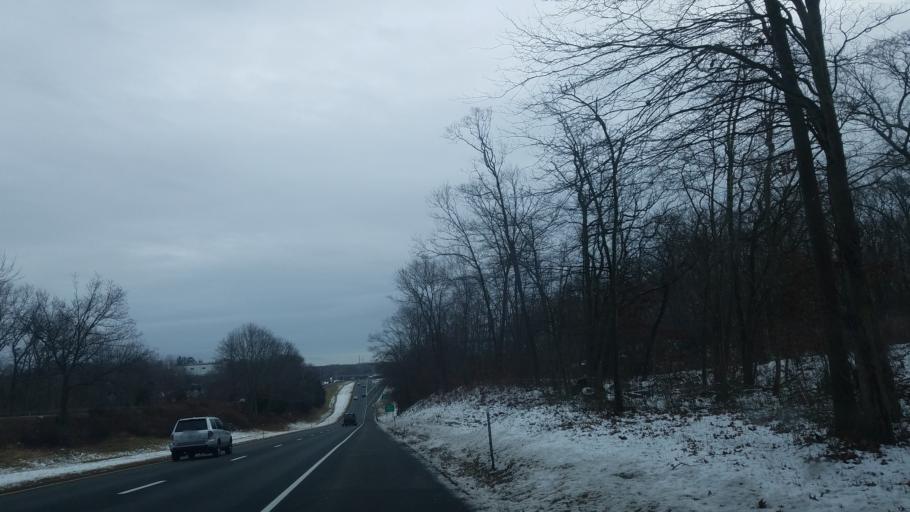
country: US
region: Connecticut
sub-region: New London County
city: Niantic
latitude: 41.3712
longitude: -72.1768
